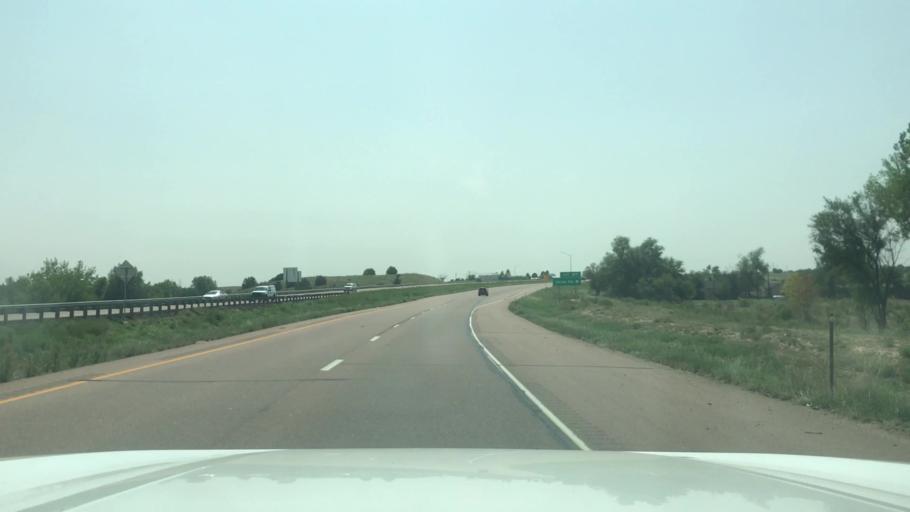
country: US
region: Colorado
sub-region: Pueblo County
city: Pueblo
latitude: 38.1202
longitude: -104.6715
